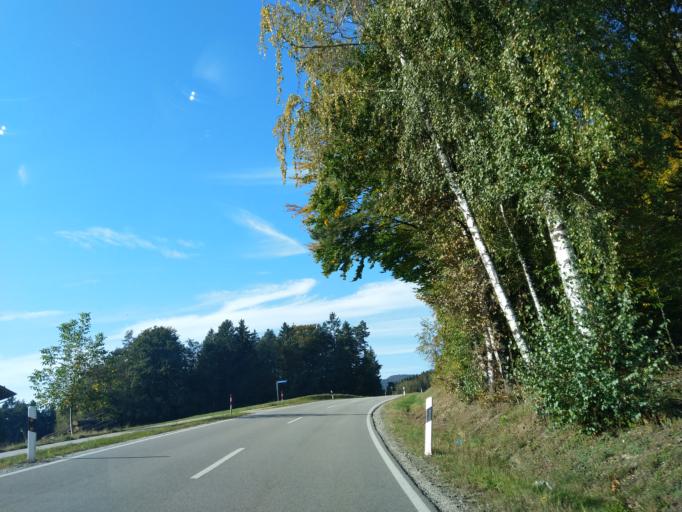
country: DE
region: Bavaria
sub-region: Lower Bavaria
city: Bernried
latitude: 48.9017
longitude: 12.8956
